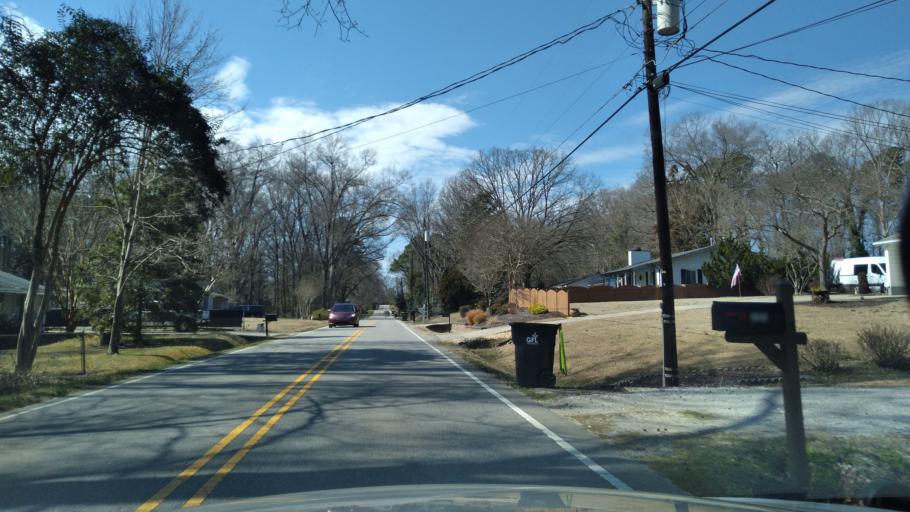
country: US
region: North Carolina
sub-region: Wake County
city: Garner
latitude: 35.7097
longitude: -78.6506
